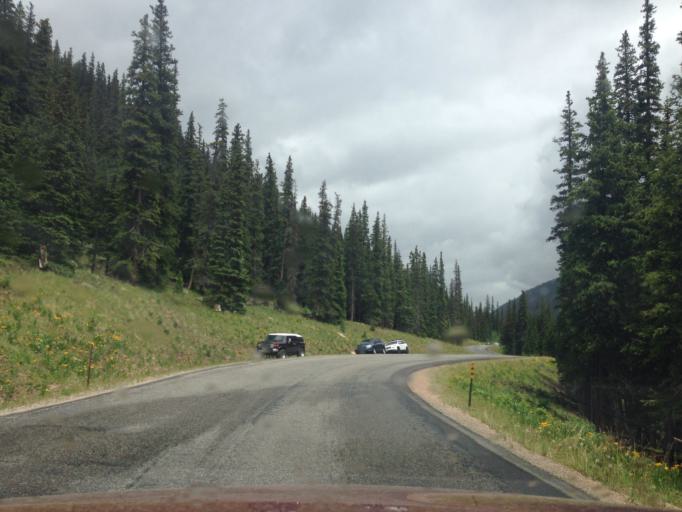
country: US
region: Colorado
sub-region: Clear Creek County
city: Georgetown
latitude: 39.6205
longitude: -105.7142
